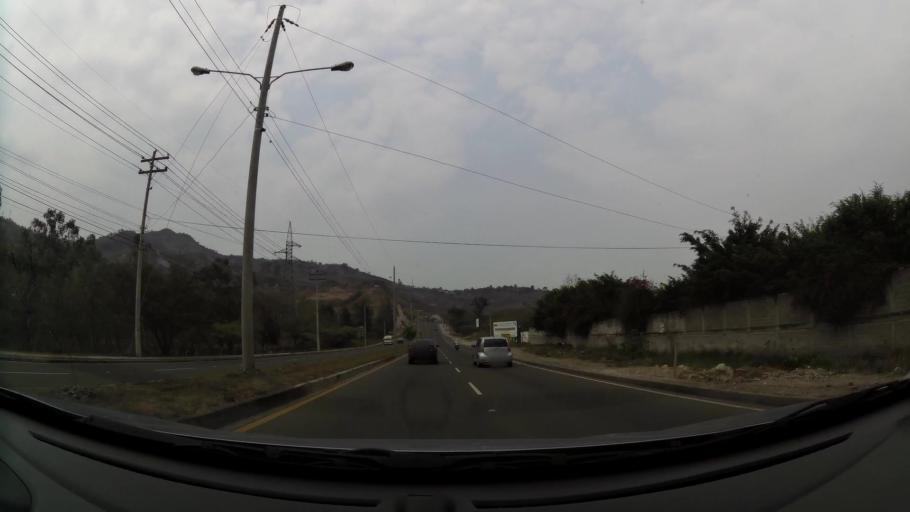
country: HN
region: Francisco Morazan
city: Tegucigalpa
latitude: 14.0661
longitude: -87.2514
